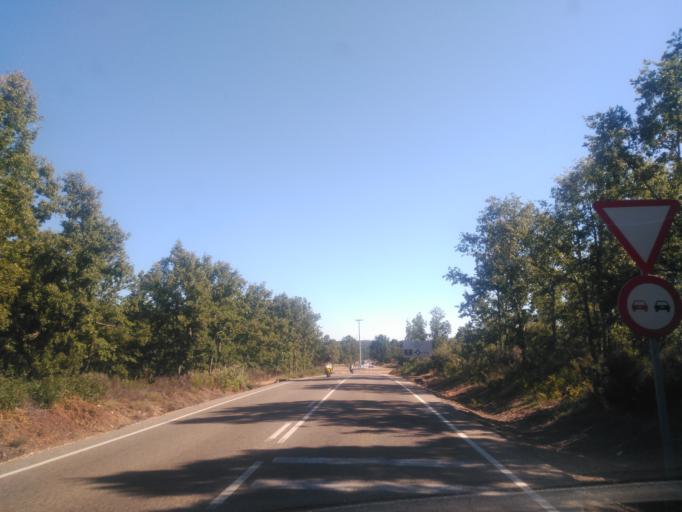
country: ES
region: Castille and Leon
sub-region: Provincia de Zamora
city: Galende
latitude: 42.0952
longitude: -6.6476
